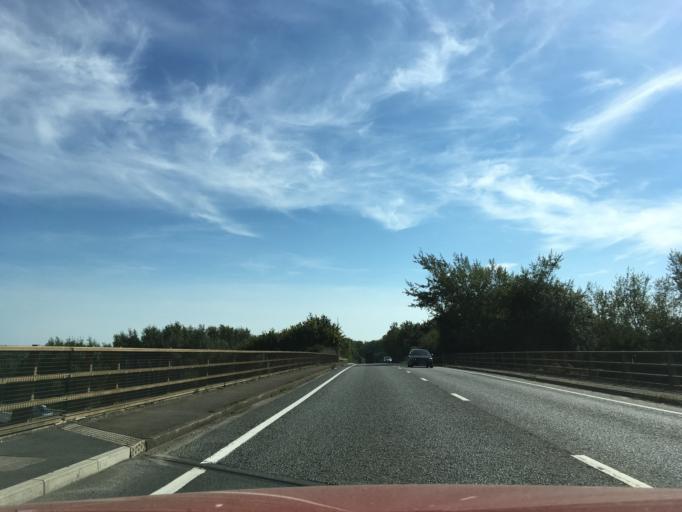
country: GB
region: England
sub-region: South Gloucestershire
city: Severn Beach
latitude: 51.5597
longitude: -2.6525
